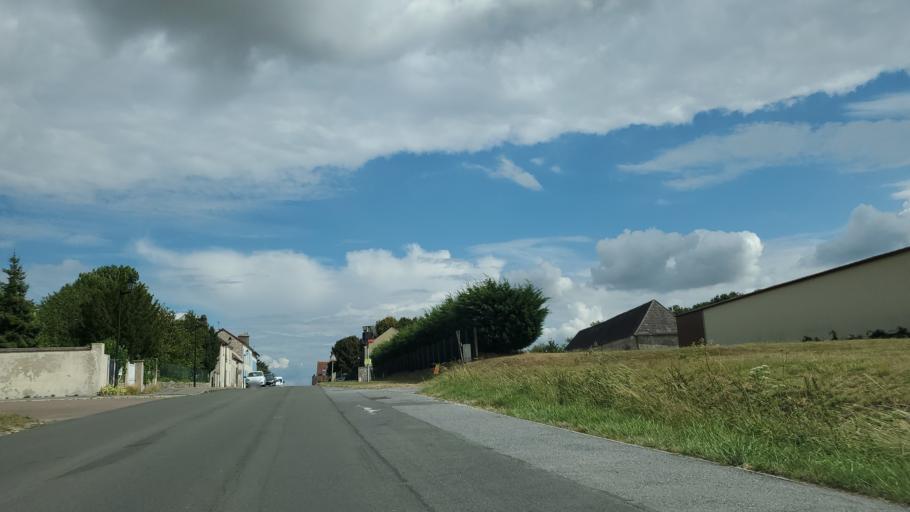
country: FR
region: Ile-de-France
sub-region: Departement de Seine-et-Marne
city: Chailly-en-Brie
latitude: 48.7909
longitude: 3.1194
